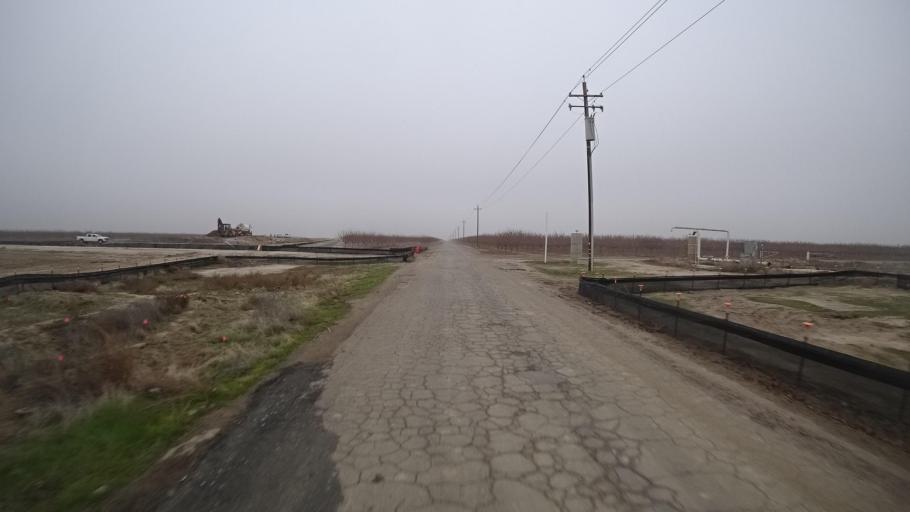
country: US
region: California
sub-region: Tulare County
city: Alpaugh
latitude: 35.7760
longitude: -119.4011
